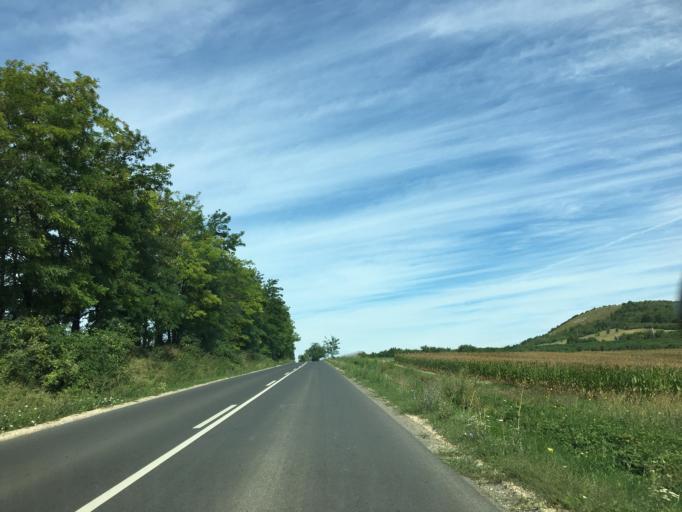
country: HU
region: Fejer
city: Many
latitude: 47.5786
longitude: 18.6740
